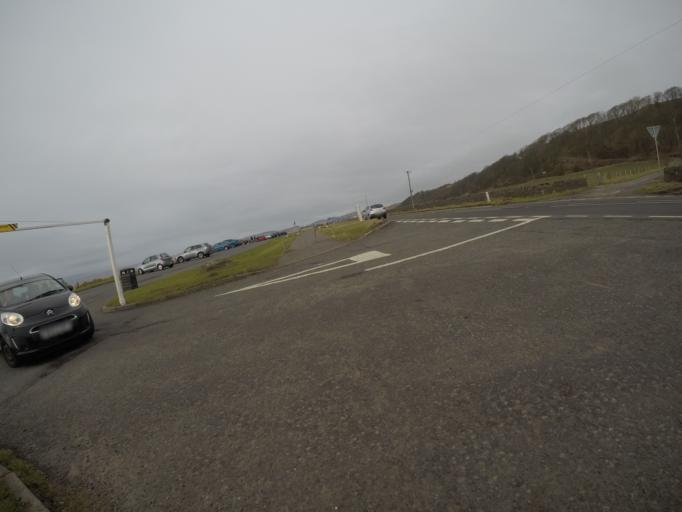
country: GB
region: Scotland
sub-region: North Ayrshire
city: West Kilbride
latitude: 55.6689
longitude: -4.8439
